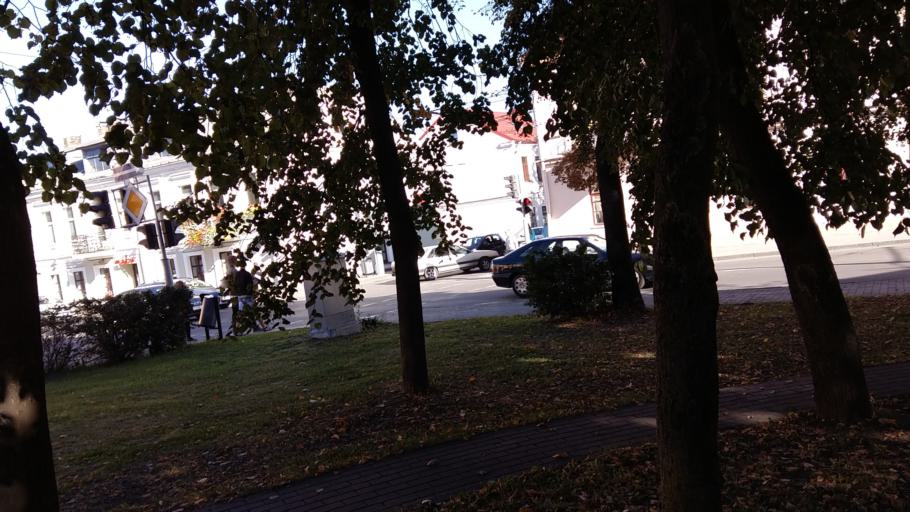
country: BY
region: Grodnenskaya
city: Hrodna
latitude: 53.6775
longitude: 23.8342
